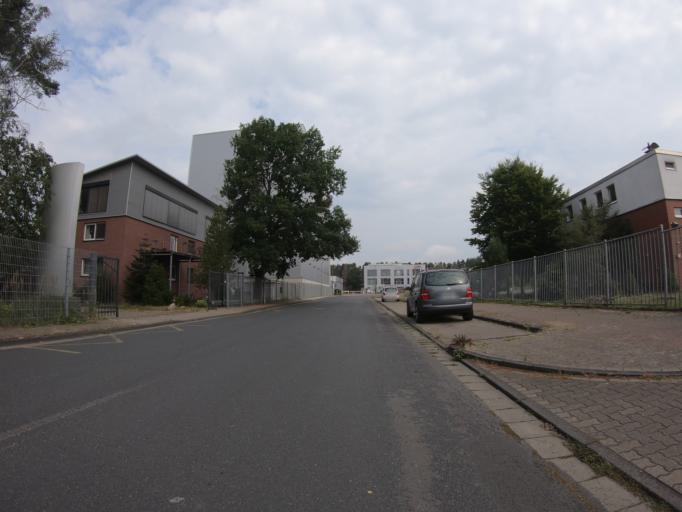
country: DE
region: Lower Saxony
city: Gifhorn
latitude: 52.4705
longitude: 10.5272
